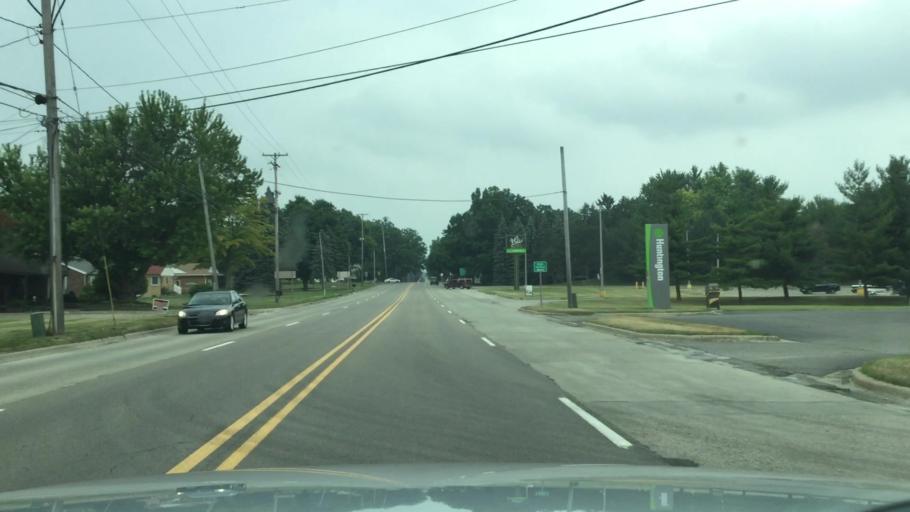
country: US
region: Michigan
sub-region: Shiawassee County
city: Owosso
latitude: 43.0148
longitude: -84.1768
